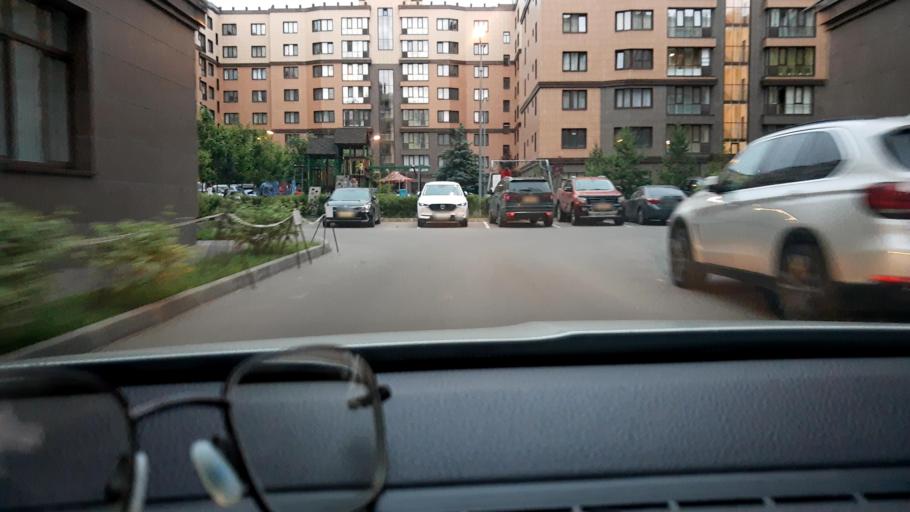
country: RU
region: Moskovskaya
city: Kommunarka
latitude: 55.5690
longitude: 37.4405
